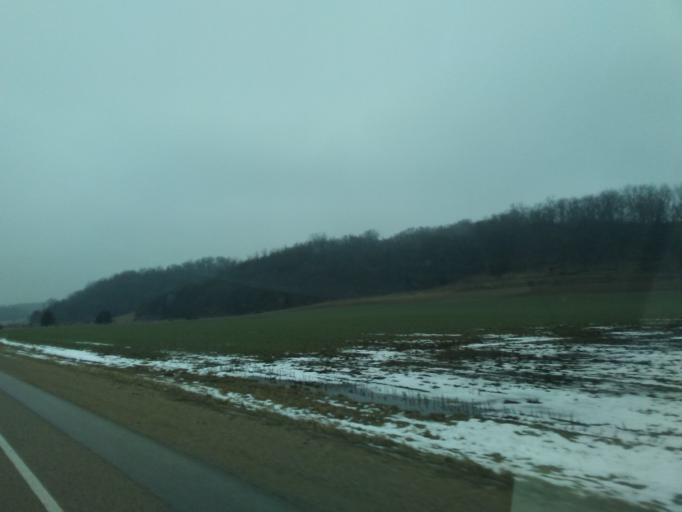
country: US
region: Wisconsin
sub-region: Dane County
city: Cross Plains
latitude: 43.1223
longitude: -89.6973
